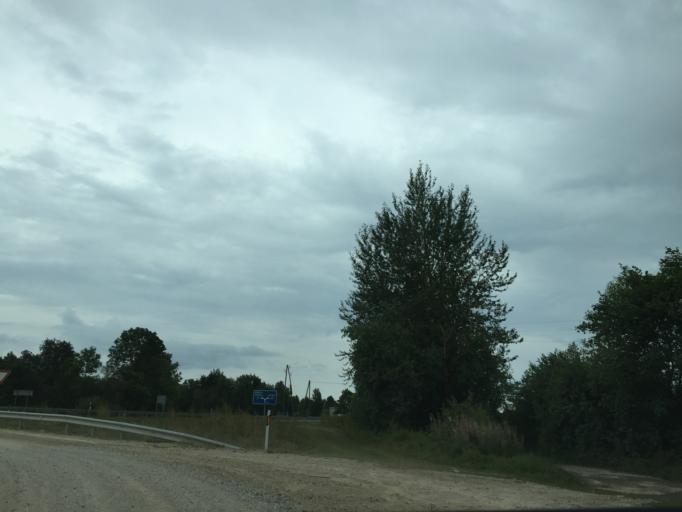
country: LV
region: Jaunpils
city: Jaunpils
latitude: 56.6763
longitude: 23.0881
